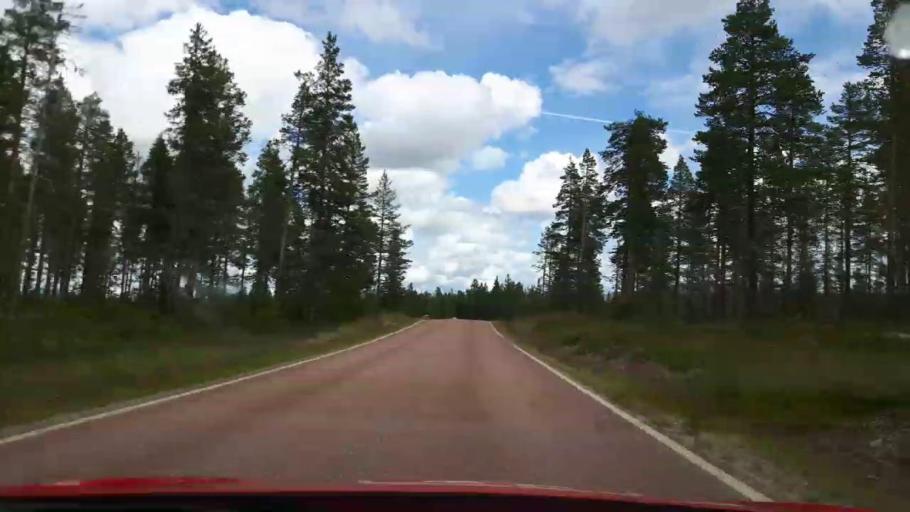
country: NO
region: Hedmark
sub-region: Trysil
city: Innbygda
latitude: 61.9192
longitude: 13.0129
